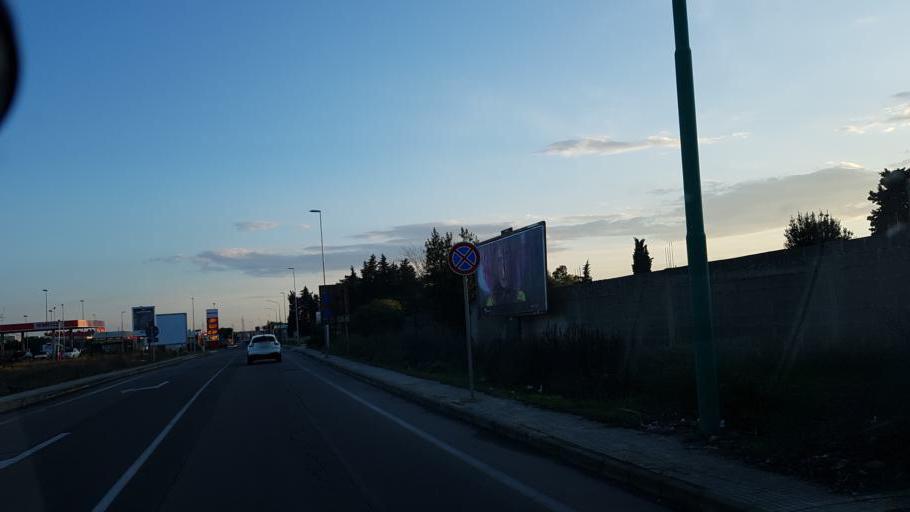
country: IT
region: Apulia
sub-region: Provincia di Lecce
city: Giorgilorio
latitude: 40.3785
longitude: 18.1405
